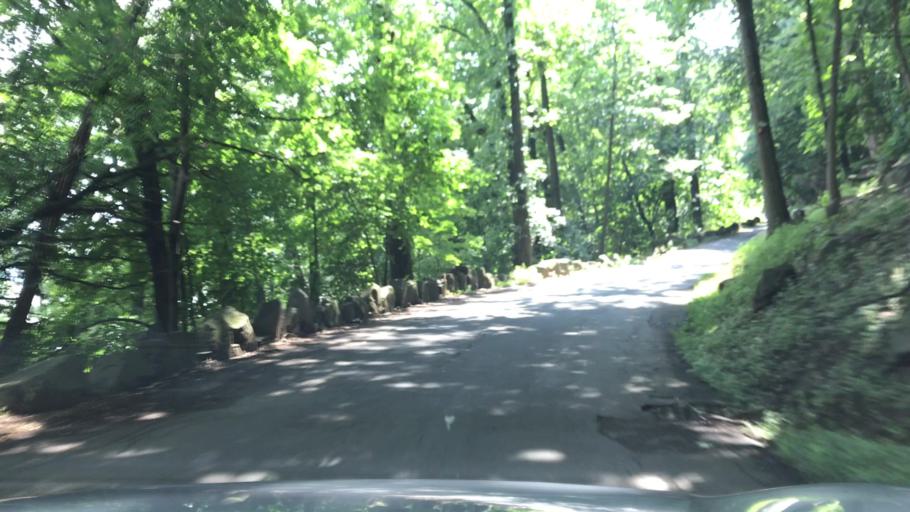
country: US
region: New Jersey
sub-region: Bergen County
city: Englewood Cliffs
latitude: 40.8841
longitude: -73.9434
